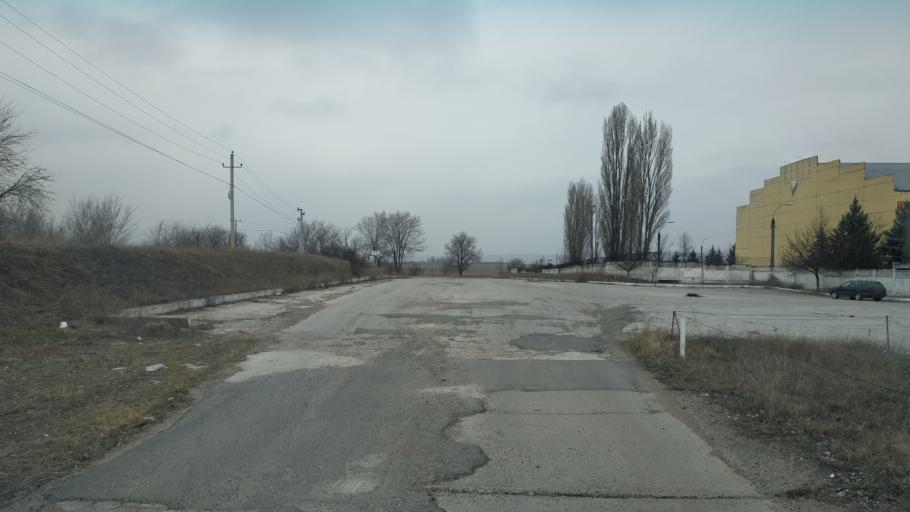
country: MD
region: Chisinau
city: Singera
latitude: 46.9128
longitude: 29.0054
